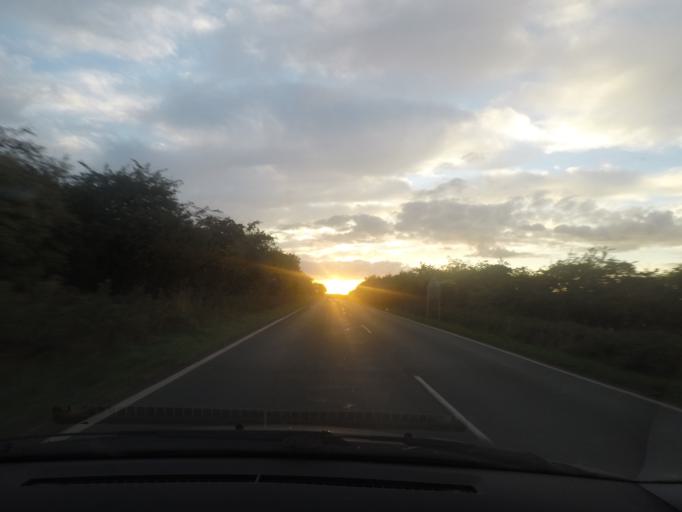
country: GB
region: England
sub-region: North Lincolnshire
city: Croxton
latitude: 53.5829
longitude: -0.3293
